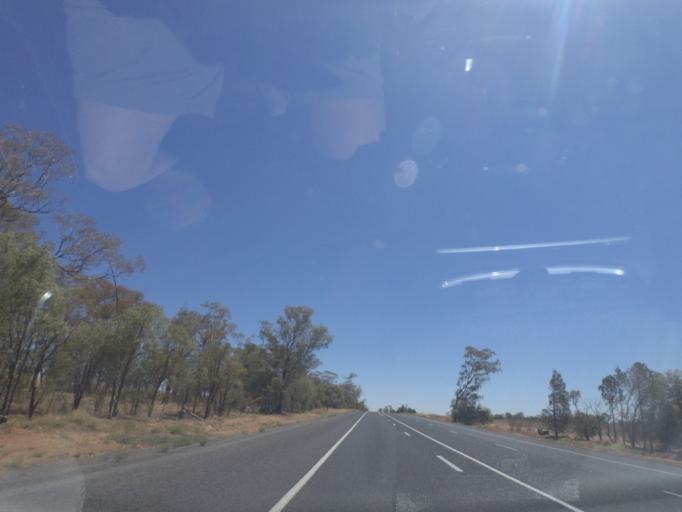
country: AU
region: New South Wales
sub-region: Gilgandra
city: Gilgandra
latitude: -31.4935
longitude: 148.8677
